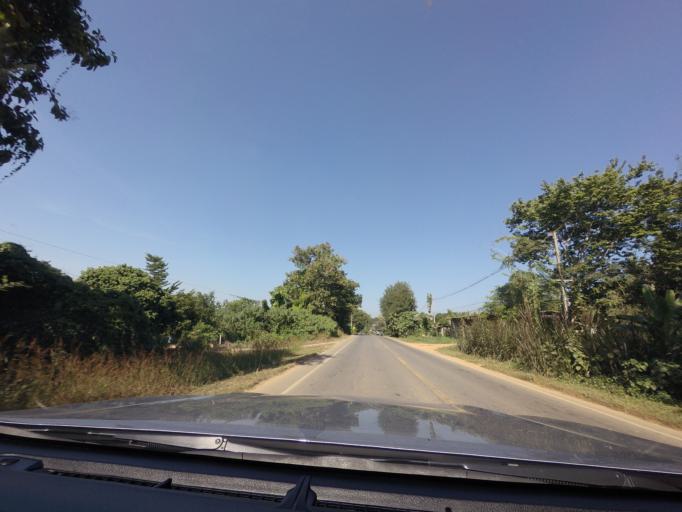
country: TH
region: Sukhothai
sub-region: Amphoe Si Satchanalai
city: Si Satchanalai
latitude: 17.6823
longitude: 99.7055
